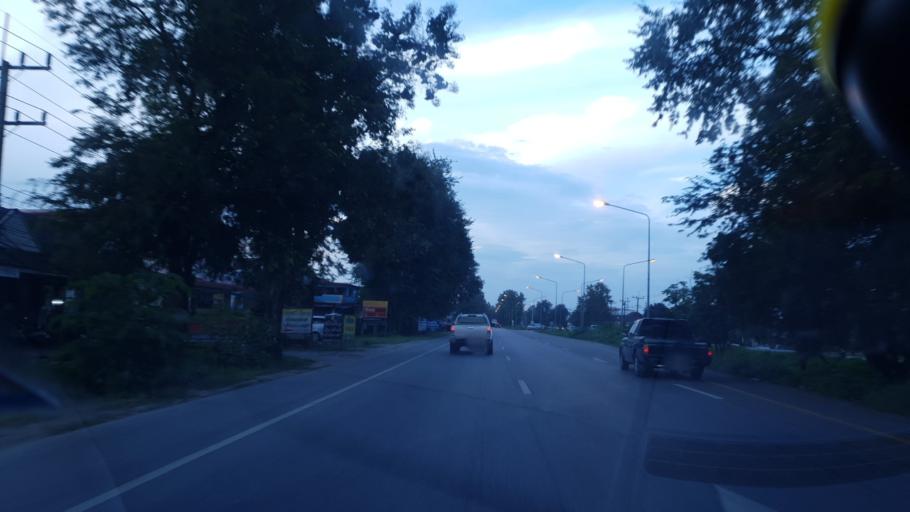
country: TH
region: Chiang Rai
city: Mae Lao
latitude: 19.7766
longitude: 99.7402
